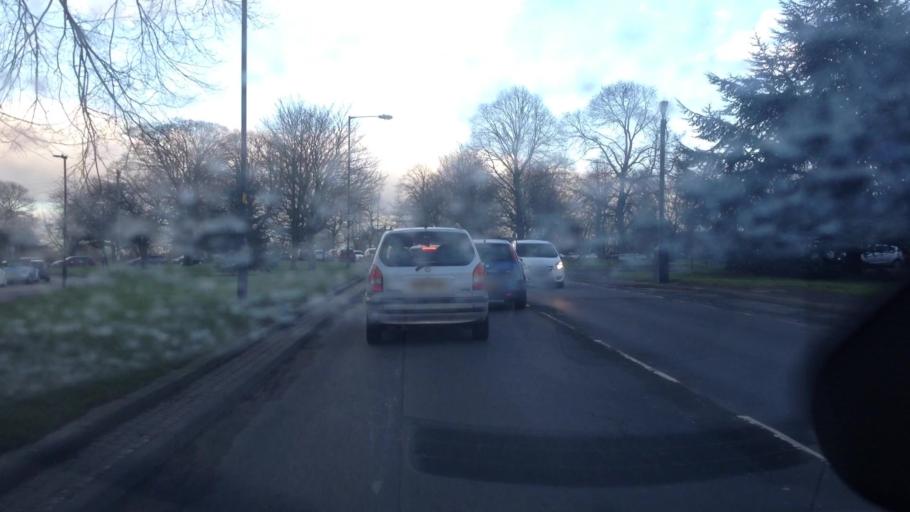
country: GB
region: England
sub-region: North Yorkshire
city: Harrogate
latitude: 53.9974
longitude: -1.5285
